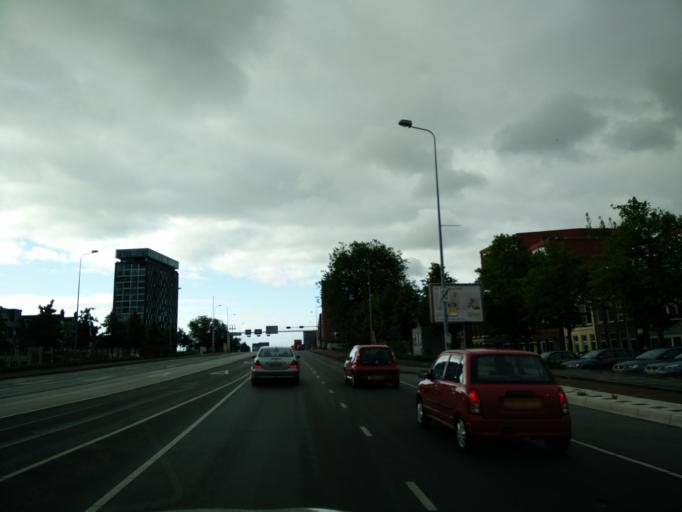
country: NL
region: Groningen
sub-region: Gemeente Groningen
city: Oosterpark
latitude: 53.2183
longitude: 6.5785
